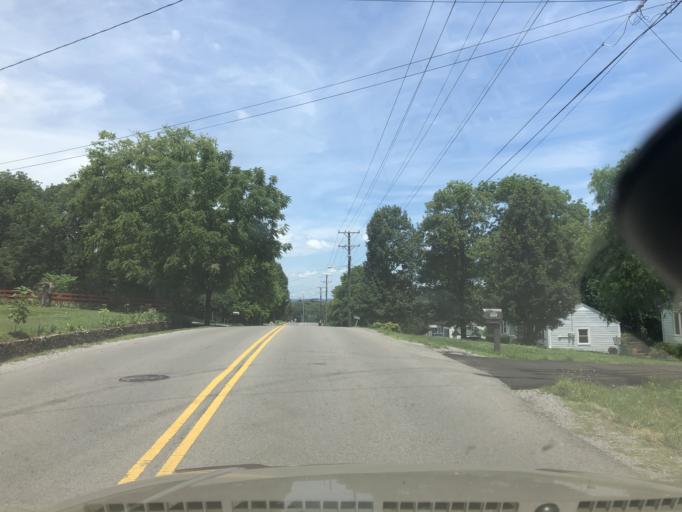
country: US
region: Tennessee
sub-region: Davidson County
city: Lakewood
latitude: 36.2600
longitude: -86.6912
